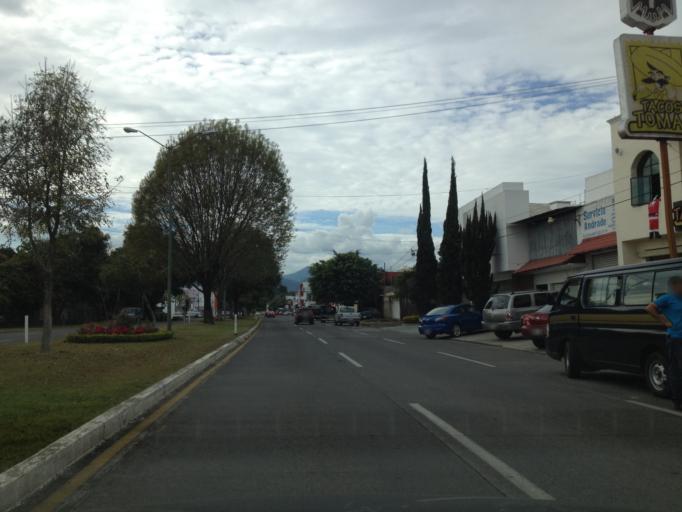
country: MX
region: Michoacan
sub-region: Uruapan
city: Uruapan
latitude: 19.4038
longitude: -102.0460
